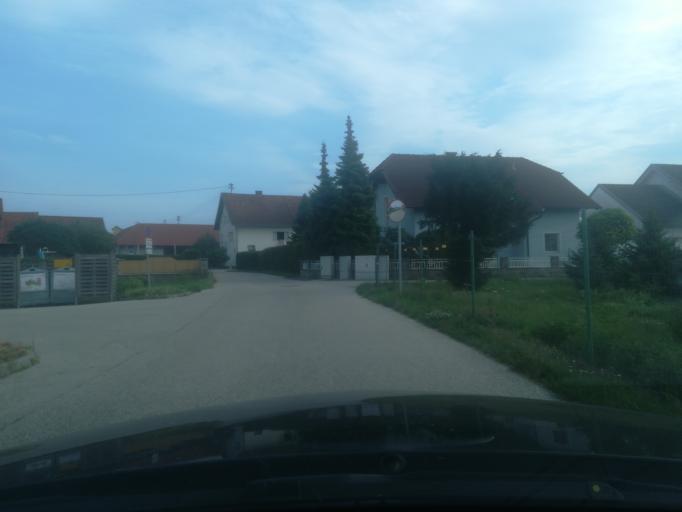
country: AT
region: Upper Austria
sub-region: Wels-Land
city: Marchtrenk
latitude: 48.1895
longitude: 14.1291
